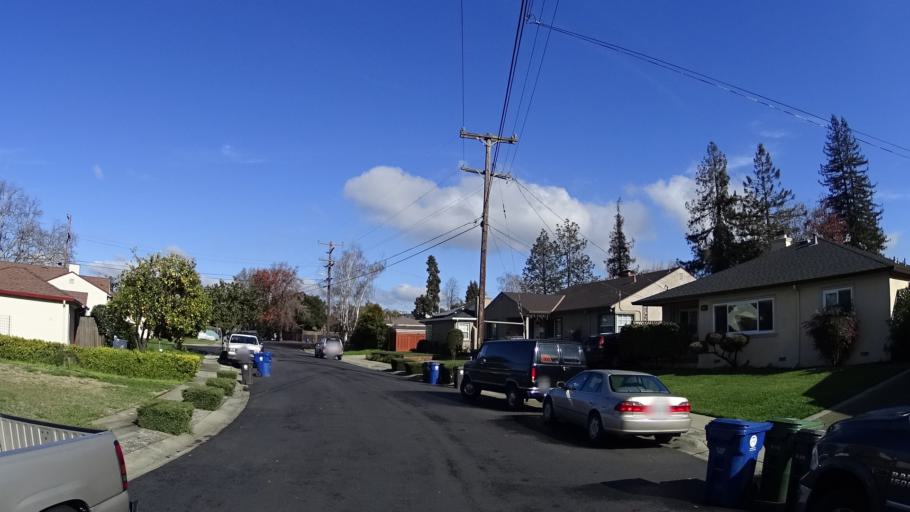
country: US
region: California
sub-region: Alameda County
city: Castro Valley
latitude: 37.6827
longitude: -122.0801
